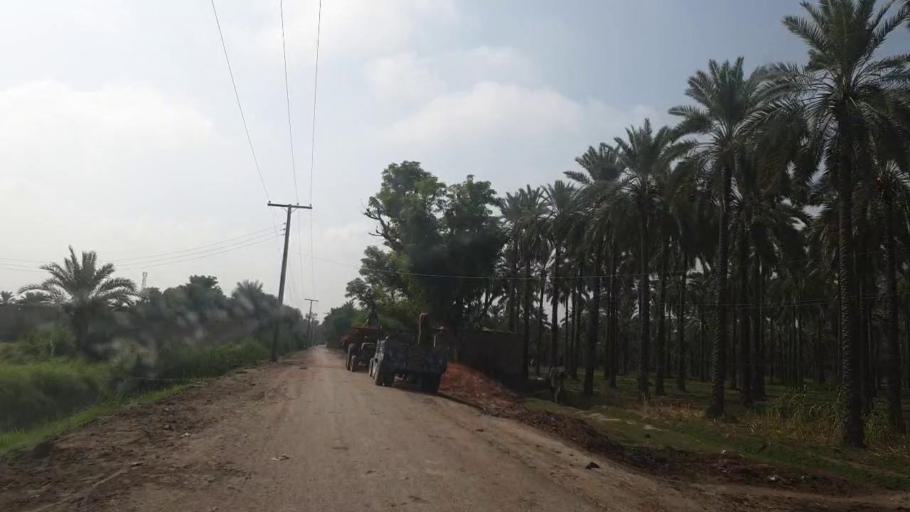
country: PK
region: Sindh
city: Khairpur
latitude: 27.5887
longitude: 68.7716
